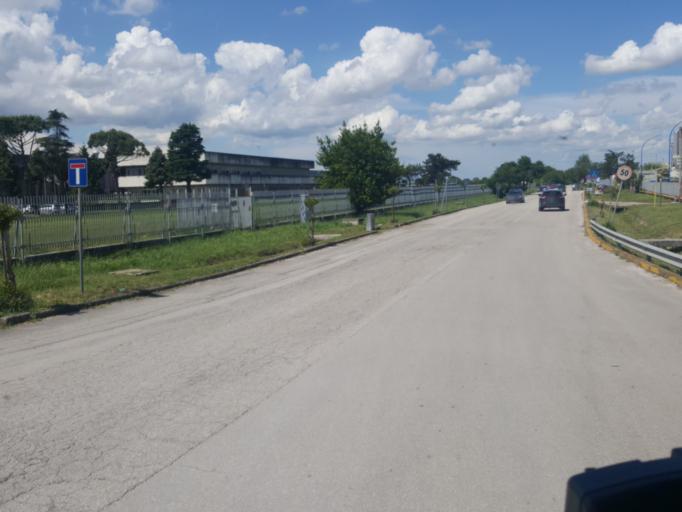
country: IT
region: Campania
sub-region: Provincia di Napoli
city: Pascarola
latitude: 40.9817
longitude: 14.3007
